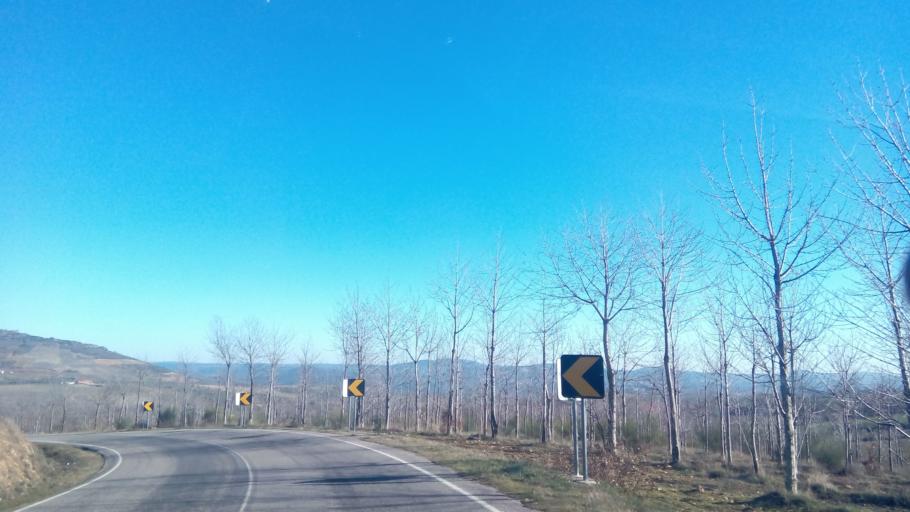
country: PT
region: Braganca
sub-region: Vimioso
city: Vimioso
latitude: 41.6724
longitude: -6.6113
